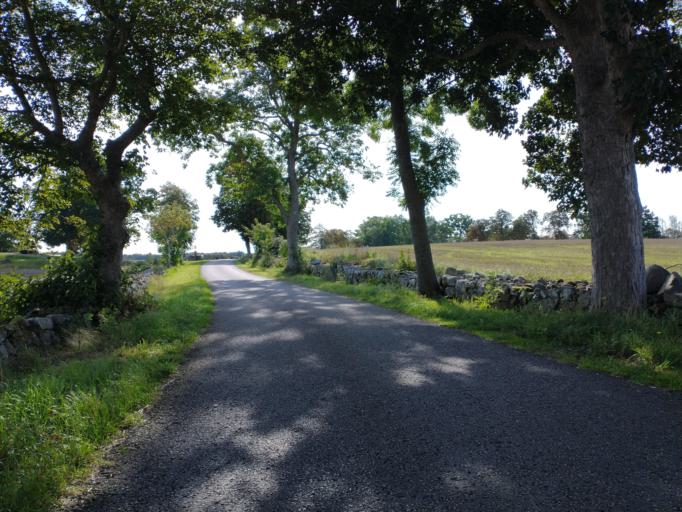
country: SE
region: Kalmar
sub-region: Kalmar Kommun
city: Lindsdal
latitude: 56.7790
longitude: 16.3213
